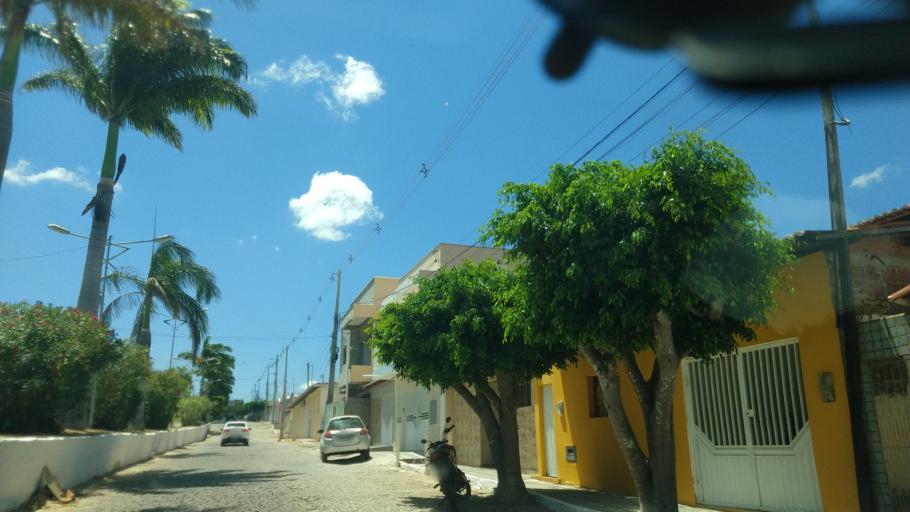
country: BR
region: Rio Grande do Norte
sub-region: Cerro Cora
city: Cerro Cora
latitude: -6.0484
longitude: -36.3508
